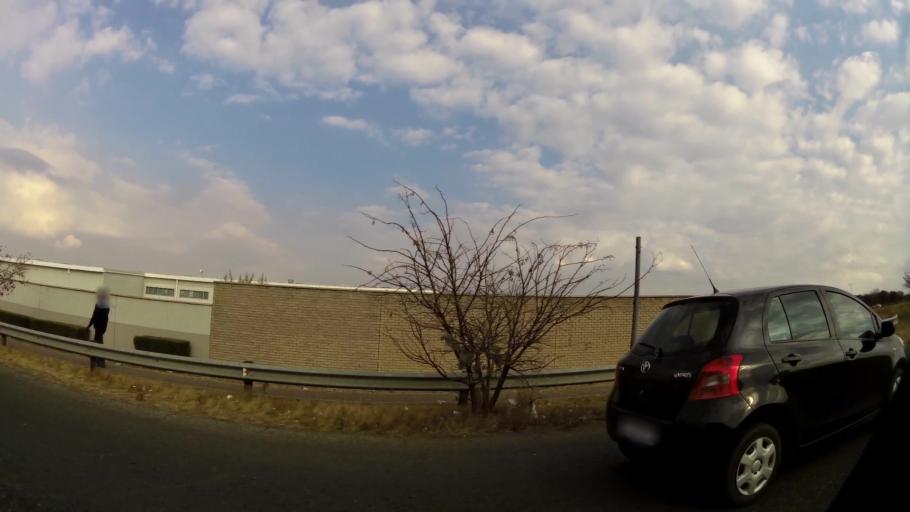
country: ZA
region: Gauteng
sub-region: Sedibeng District Municipality
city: Vanderbijlpark
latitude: -26.6988
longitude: 27.8803
